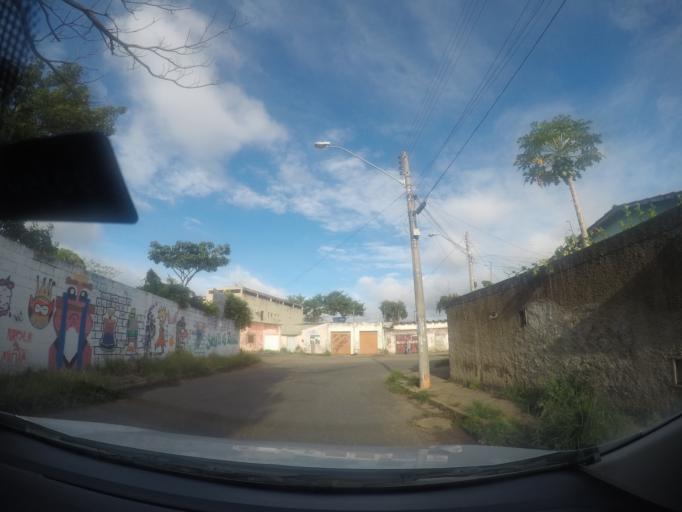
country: BR
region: Goias
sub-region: Goiania
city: Goiania
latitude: -16.6890
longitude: -49.3147
